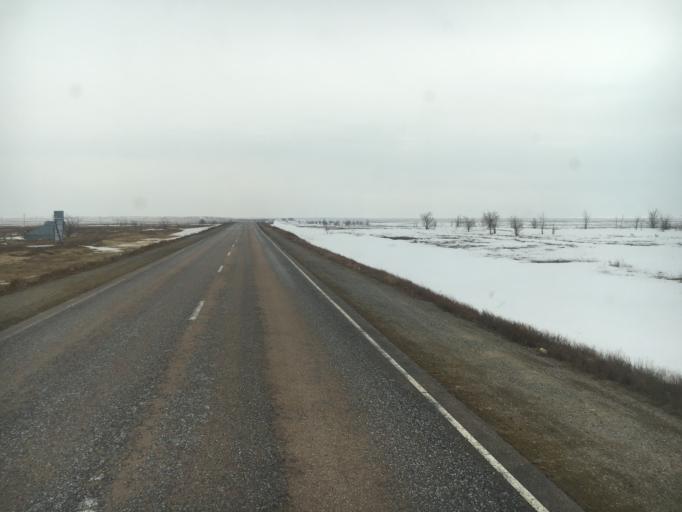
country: RU
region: Orenburg
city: Dombarovskiy
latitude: 50.0935
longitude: 59.4910
